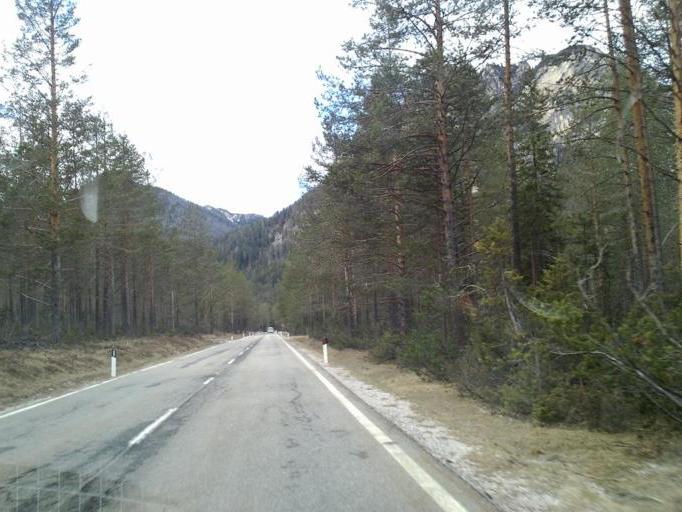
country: IT
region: Trentino-Alto Adige
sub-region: Bolzano
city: Dobbiaco
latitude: 46.6150
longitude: 12.2238
